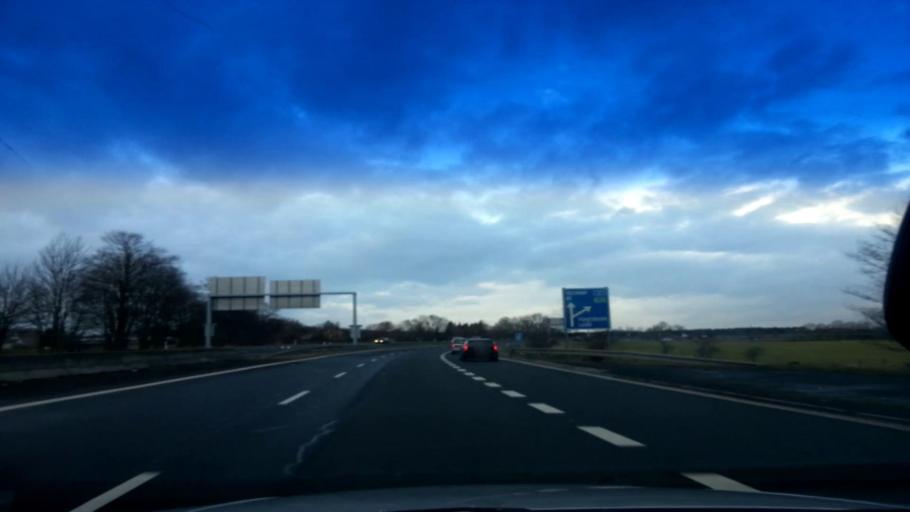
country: CZ
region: Karlovarsky
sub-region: Okres Cheb
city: Cheb
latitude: 50.1003
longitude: 12.3662
